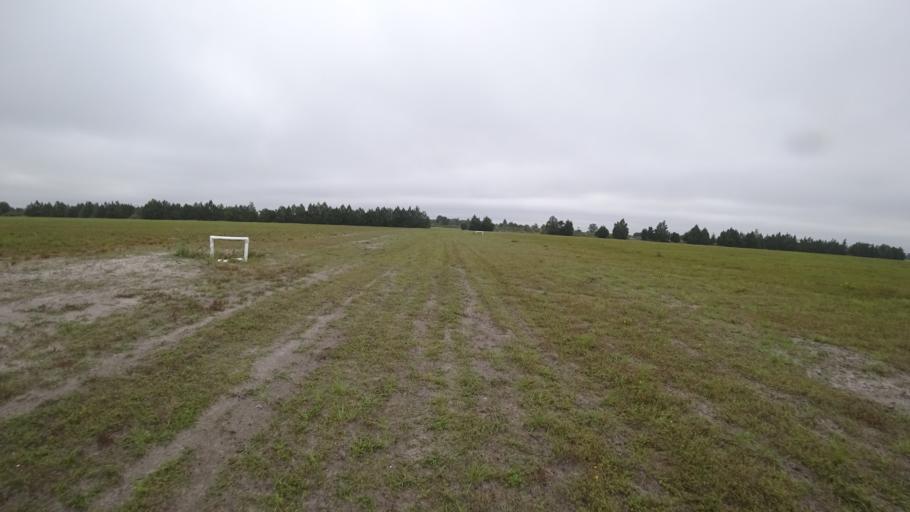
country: US
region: Florida
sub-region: Sarasota County
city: Warm Mineral Springs
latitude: 27.3077
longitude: -82.1512
